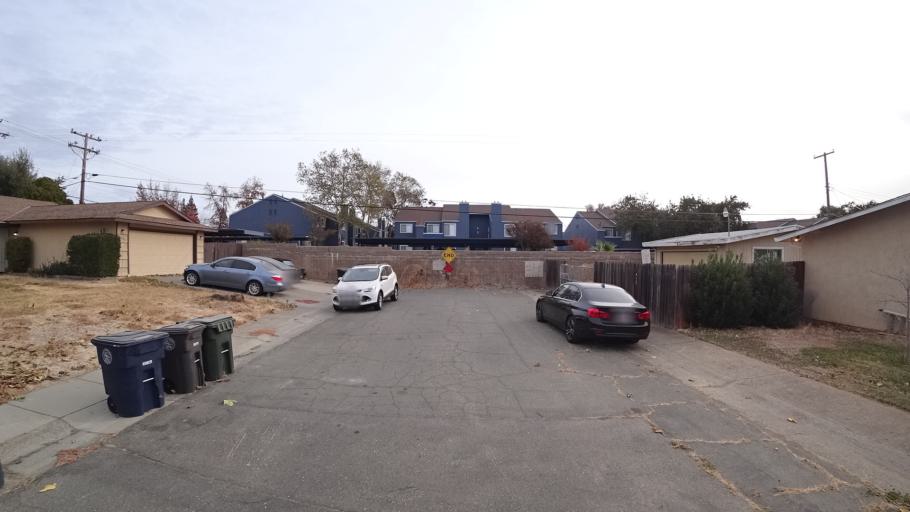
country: US
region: California
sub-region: Sacramento County
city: Citrus Heights
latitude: 38.7180
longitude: -121.2940
